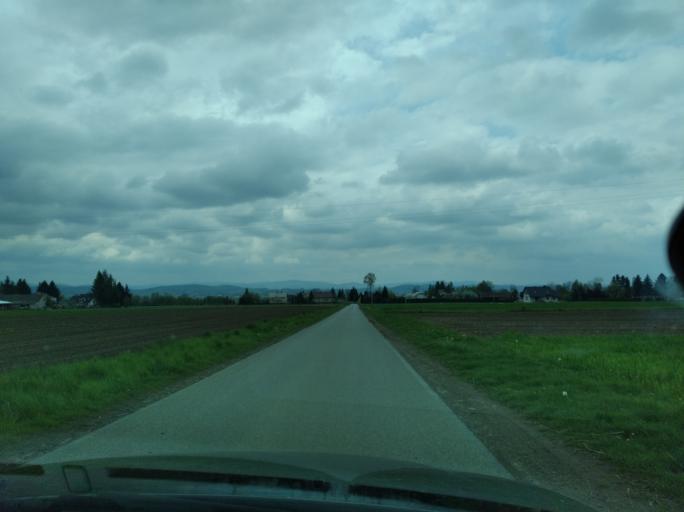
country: PL
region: Subcarpathian Voivodeship
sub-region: Powiat sanocki
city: Zarszyn
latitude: 49.6212
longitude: 22.0106
